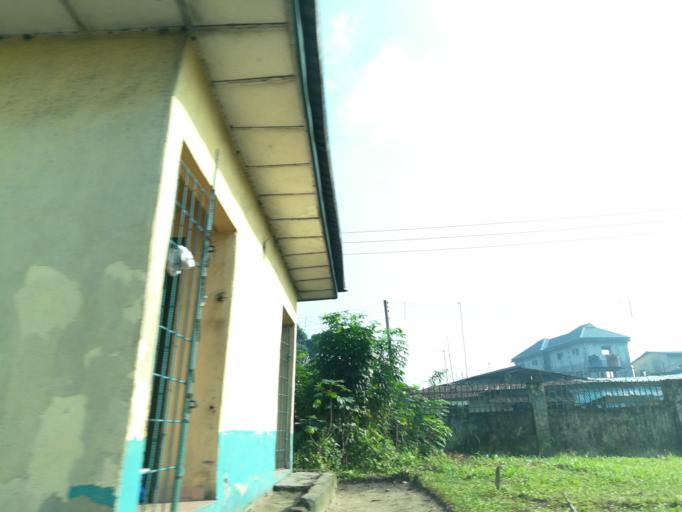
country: NG
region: Rivers
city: Port Harcourt
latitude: 4.8147
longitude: 7.0207
